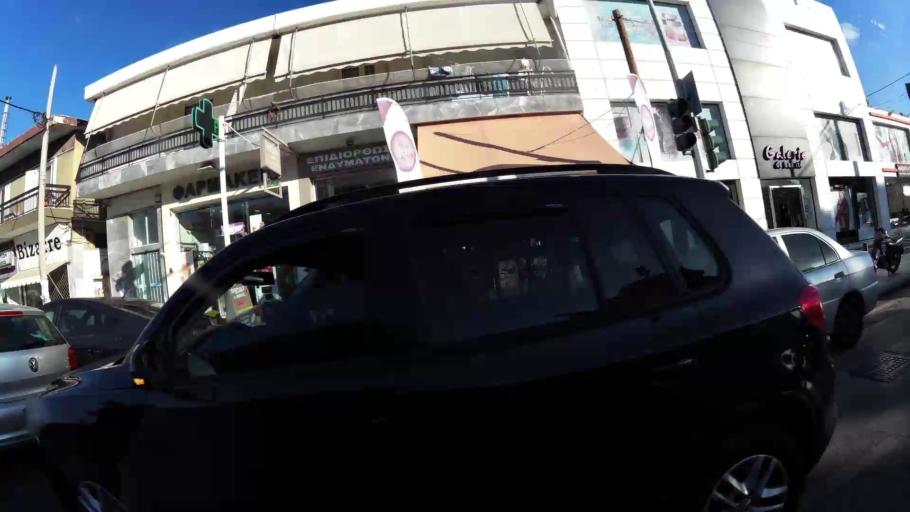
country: GR
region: Attica
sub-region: Nomarchia Athinas
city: Melissia
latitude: 38.0512
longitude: 23.8342
